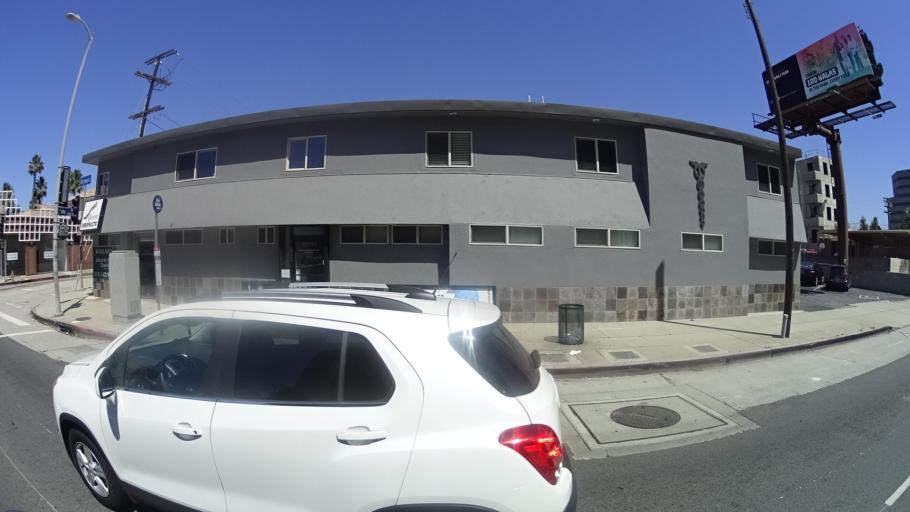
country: US
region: California
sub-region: Los Angeles County
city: Westwood, Los Angeles
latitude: 34.0362
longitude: -118.4448
